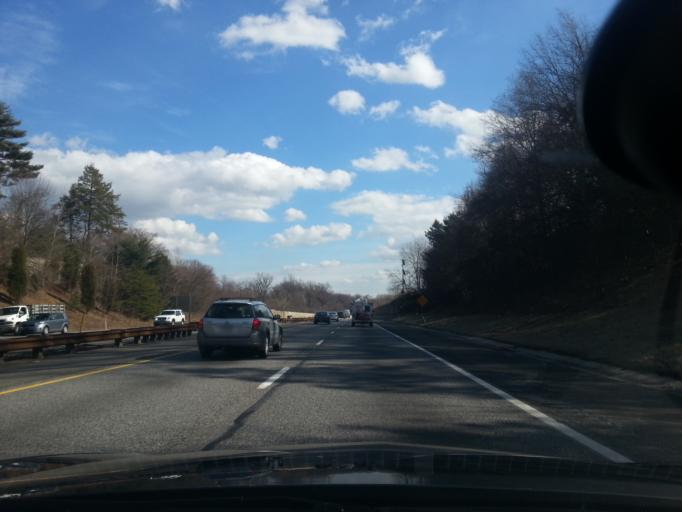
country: US
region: Pennsylvania
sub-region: Delaware County
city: Swarthmore
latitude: 39.9008
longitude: -75.3626
